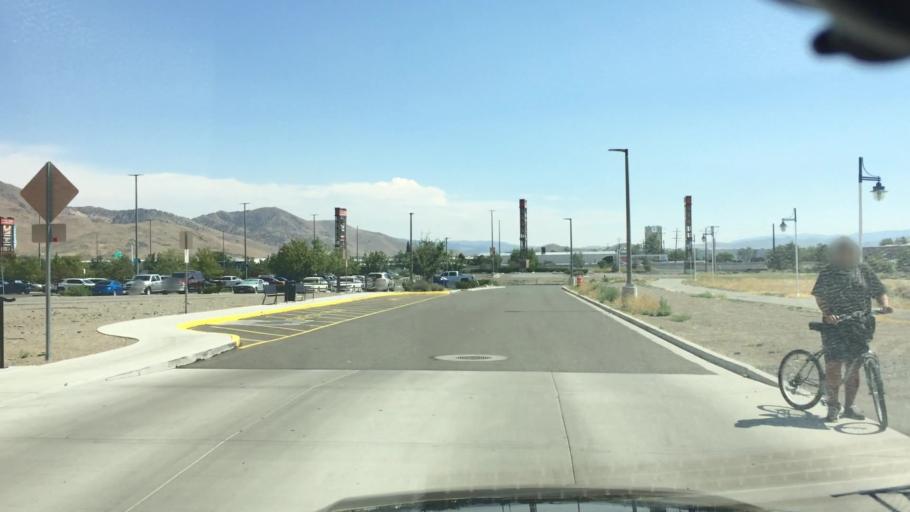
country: US
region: Nevada
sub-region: Washoe County
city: Sparks
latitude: 39.5315
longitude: -119.7238
